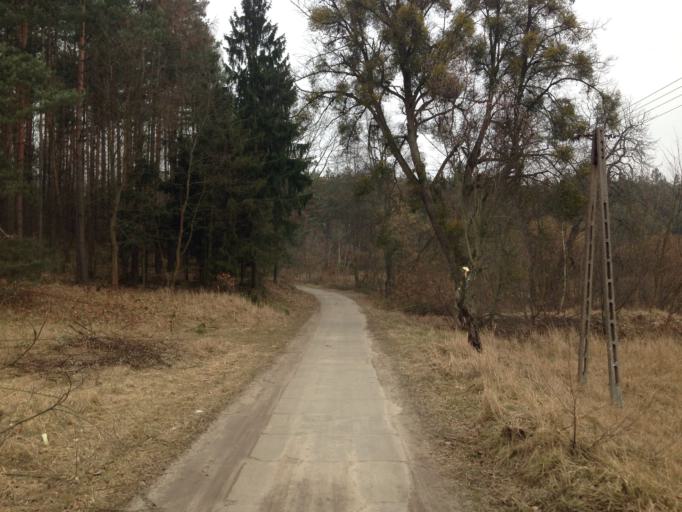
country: PL
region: Pomeranian Voivodeship
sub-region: Powiat kwidzynski
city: Sadlinki
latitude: 53.7212
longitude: 18.8126
